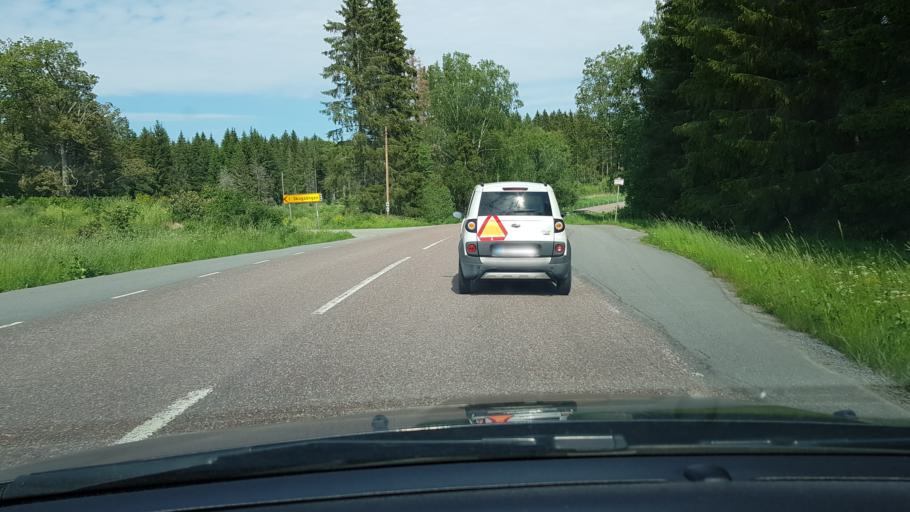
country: SE
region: Uppsala
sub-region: Knivsta Kommun
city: Knivsta
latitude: 59.8598
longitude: 17.9101
